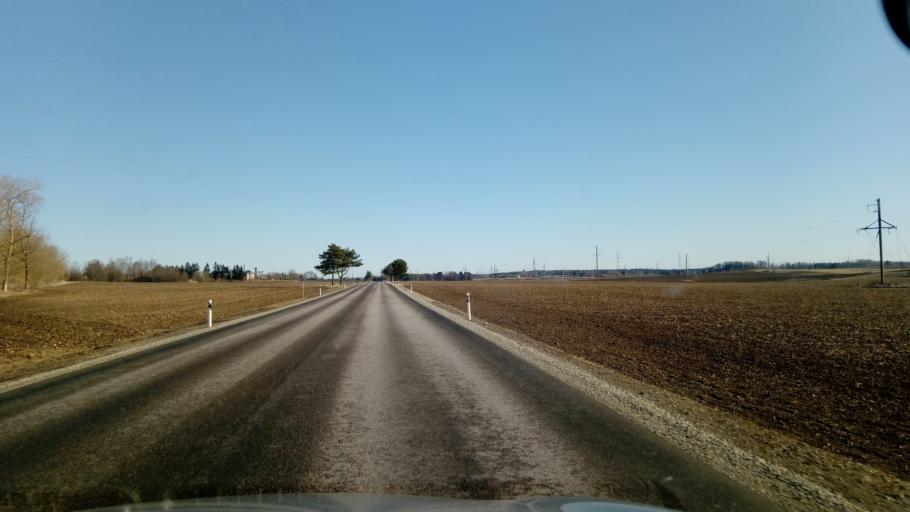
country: EE
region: Laeaene-Virumaa
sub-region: Rakvere linn
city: Rakvere
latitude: 59.3038
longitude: 26.3190
